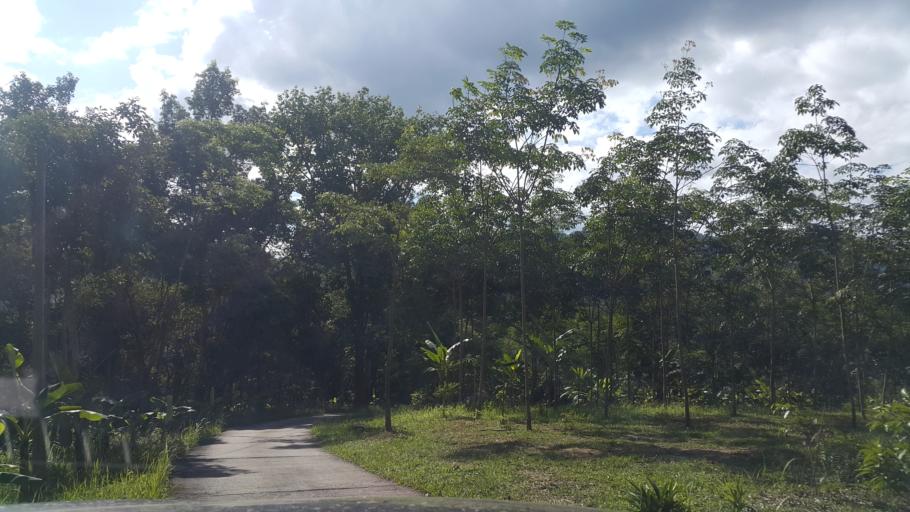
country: TH
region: Loei
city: Na Haeo
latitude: 17.5609
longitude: 100.9528
